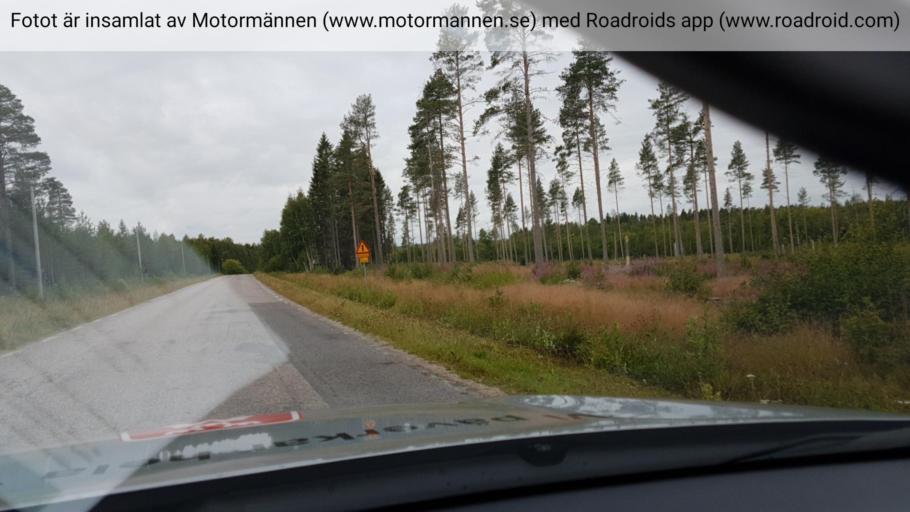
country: SE
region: Norrbotten
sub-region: Bodens Kommun
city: Saevast
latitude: 65.6699
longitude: 21.7848
